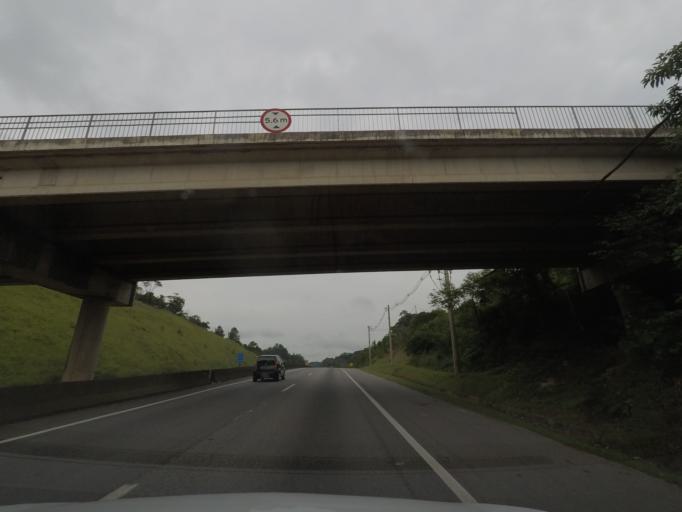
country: BR
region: Sao Paulo
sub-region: Juquitiba
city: Juquitiba
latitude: -23.9561
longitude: -47.1110
